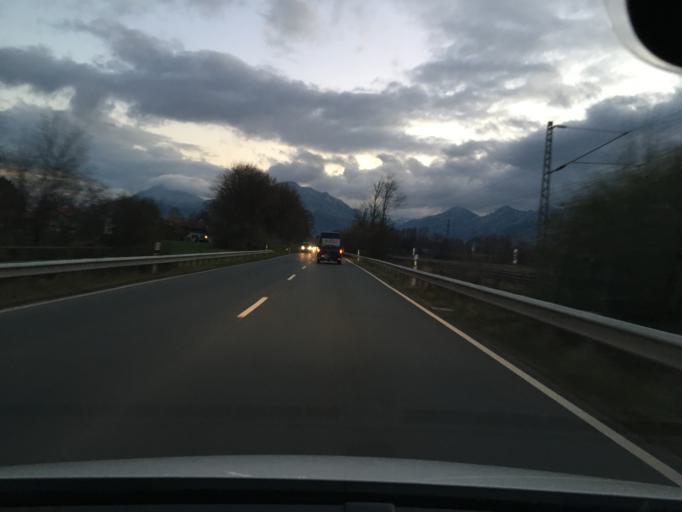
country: DE
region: Bavaria
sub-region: Upper Bavaria
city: Raubling
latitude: 47.7795
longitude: 12.1051
